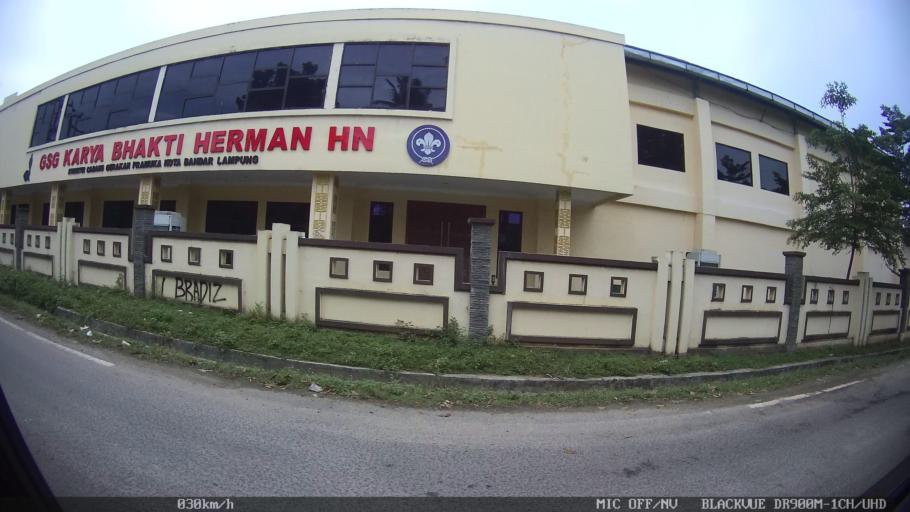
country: ID
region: Lampung
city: Kedaton
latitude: -5.3740
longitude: 105.2184
